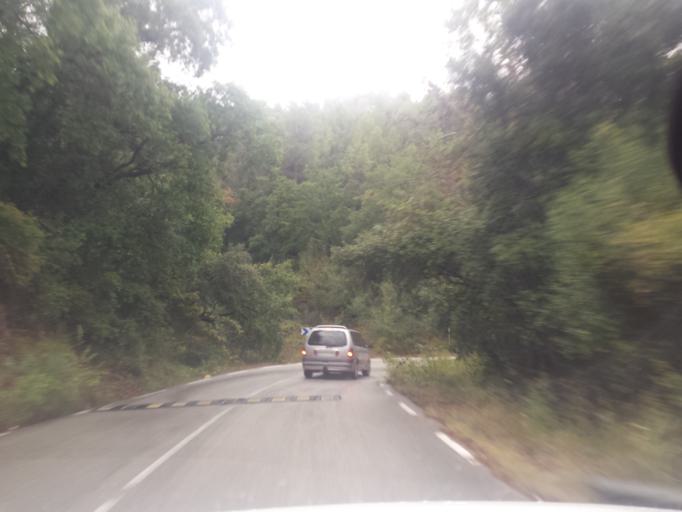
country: ES
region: Catalonia
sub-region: Provincia de Barcelona
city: Sant Andreu de la Barca
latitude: 41.4432
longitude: 1.9500
